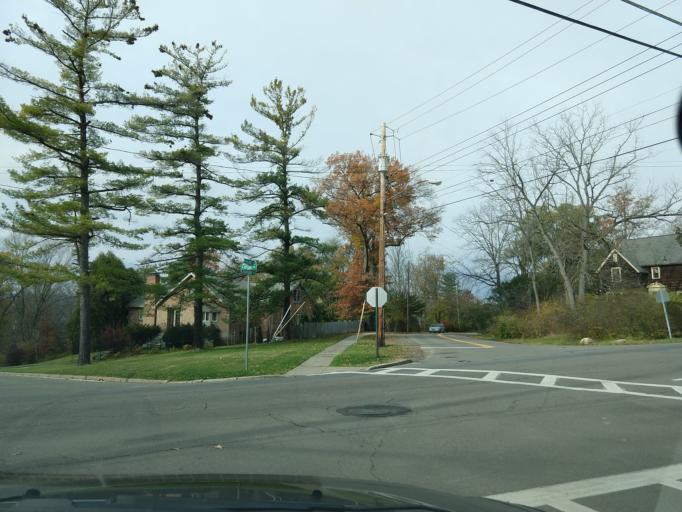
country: US
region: New York
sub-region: Tompkins County
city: Cayuga Heights
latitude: 42.4651
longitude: -76.4901
